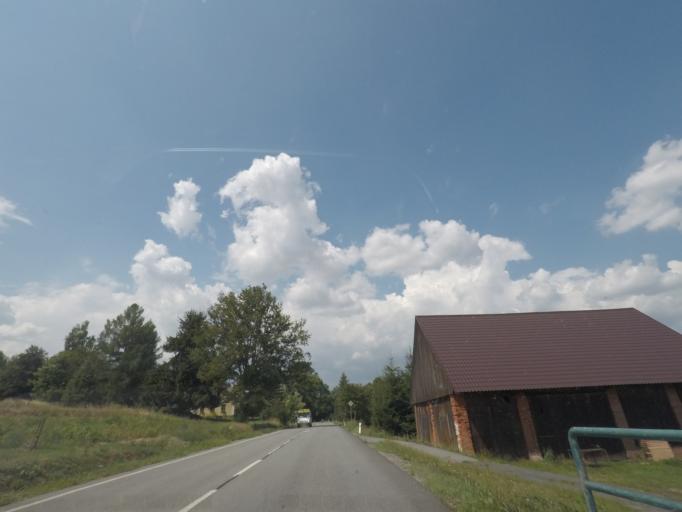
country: CZ
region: Kralovehradecky
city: Zadni Mostek
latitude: 50.5273
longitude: 15.6860
